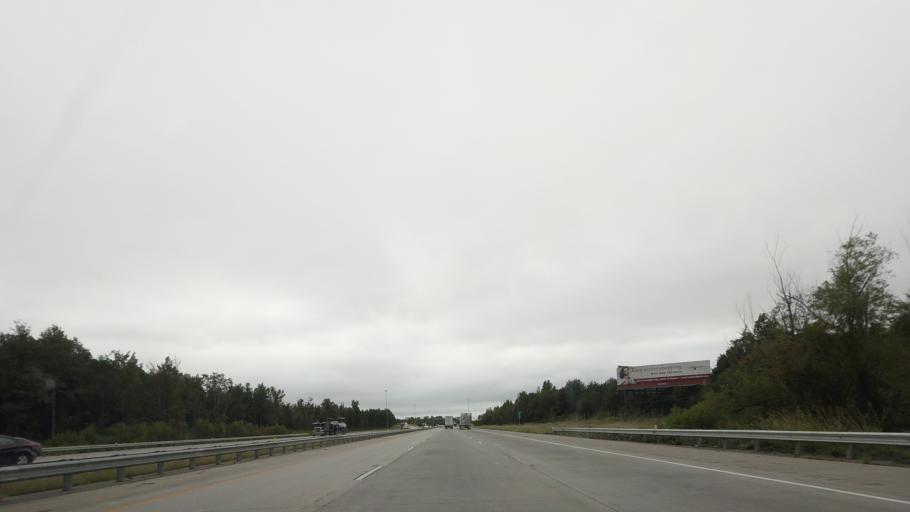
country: US
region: Georgia
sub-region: Dooly County
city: Unadilla
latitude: 32.1975
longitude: -83.7472
